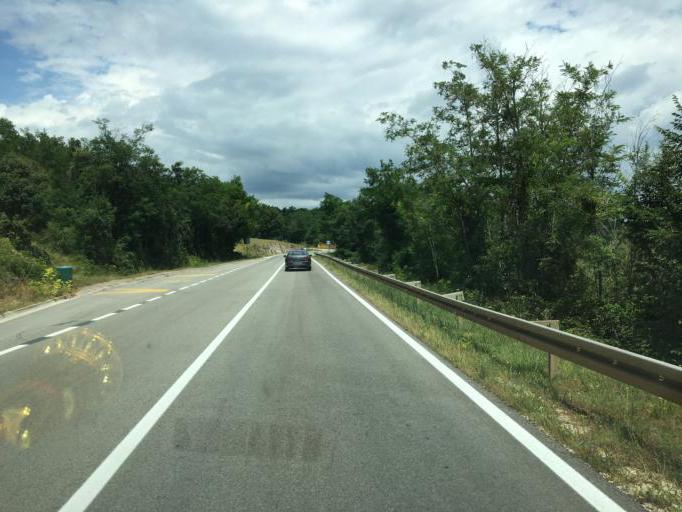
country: HR
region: Istarska
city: Karojba
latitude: 45.2322
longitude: 13.8417
